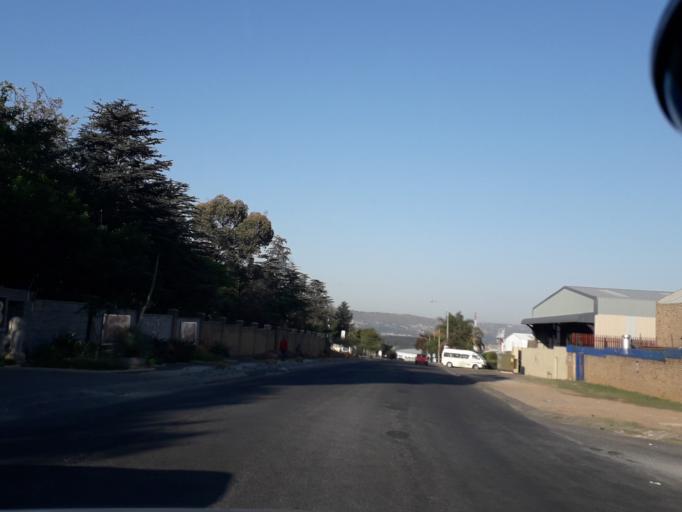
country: ZA
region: Gauteng
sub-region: West Rand District Municipality
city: Muldersdriseloop
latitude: -26.0805
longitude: 27.9185
